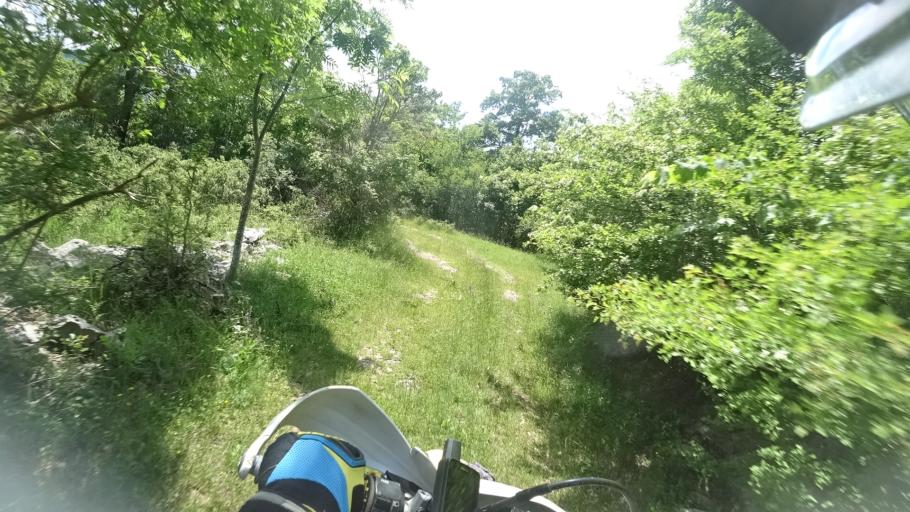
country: HR
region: Zadarska
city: Gracac
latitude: 44.3656
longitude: 15.9460
